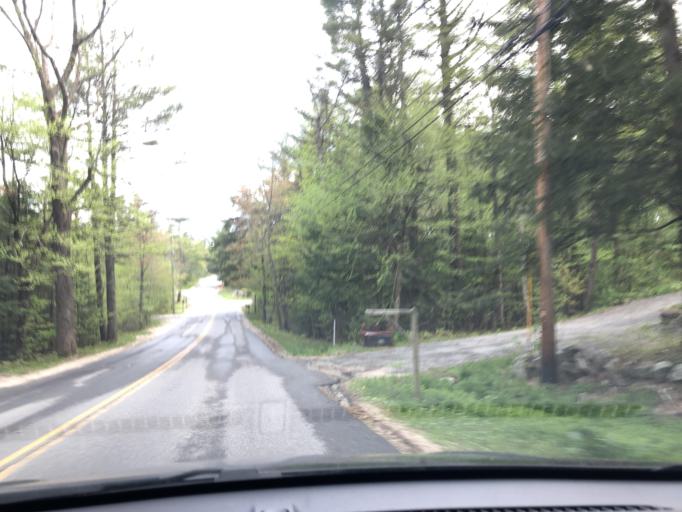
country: US
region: New Hampshire
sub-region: Merrimack County
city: New London
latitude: 43.4145
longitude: -72.0069
